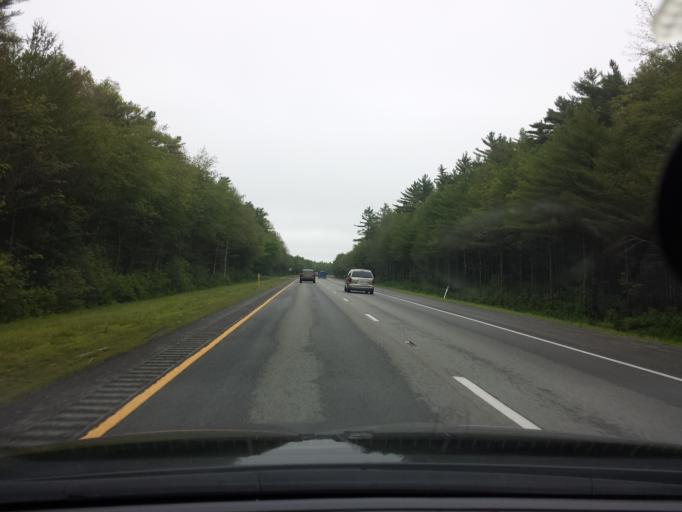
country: US
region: Massachusetts
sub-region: Plymouth County
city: Mattapoisett Center
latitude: 41.6999
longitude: -70.7995
